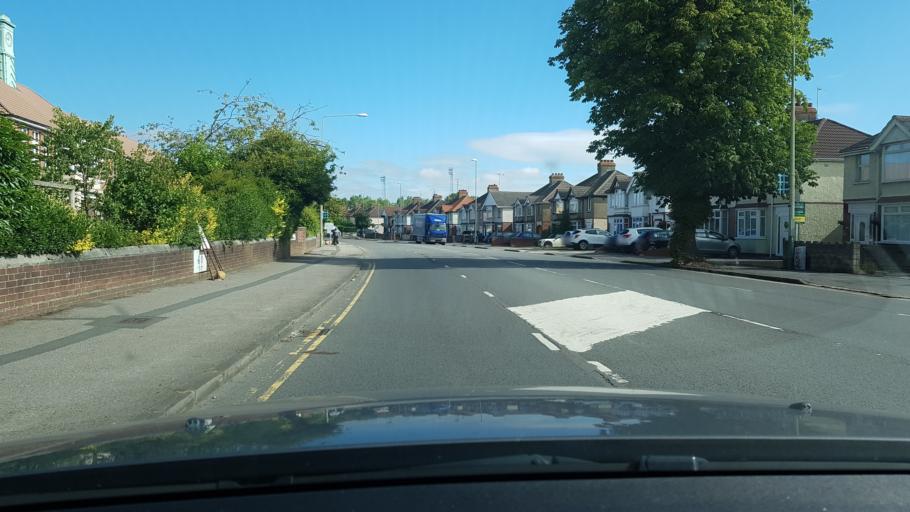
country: GB
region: England
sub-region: Borough of Swindon
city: Swindon
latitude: 51.5603
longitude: -1.7712
